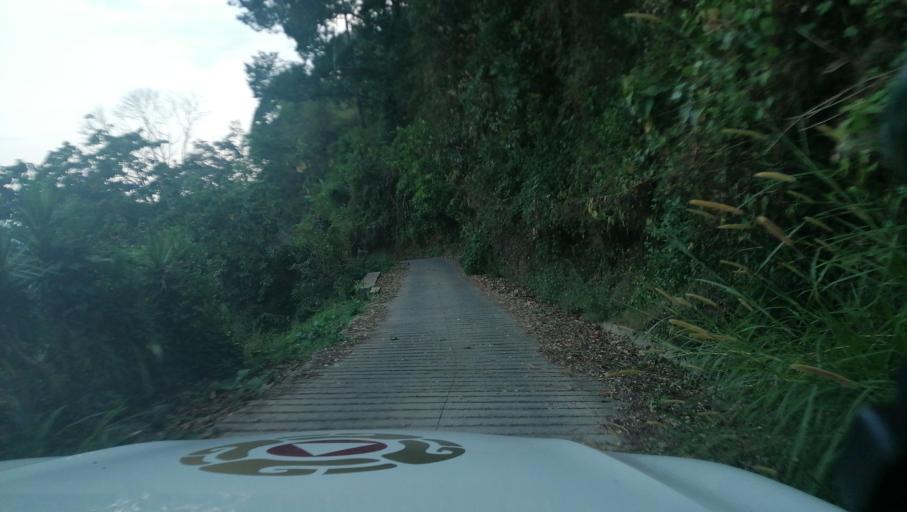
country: MX
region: Chiapas
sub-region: Cacahoatan
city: Benito Juarez
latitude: 15.0947
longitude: -92.2202
